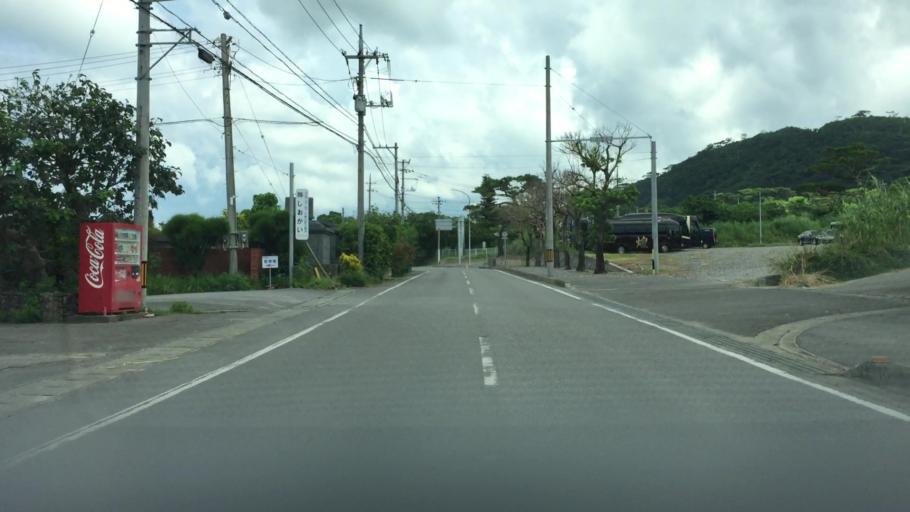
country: JP
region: Okinawa
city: Ishigaki
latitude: 24.3635
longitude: 124.1424
